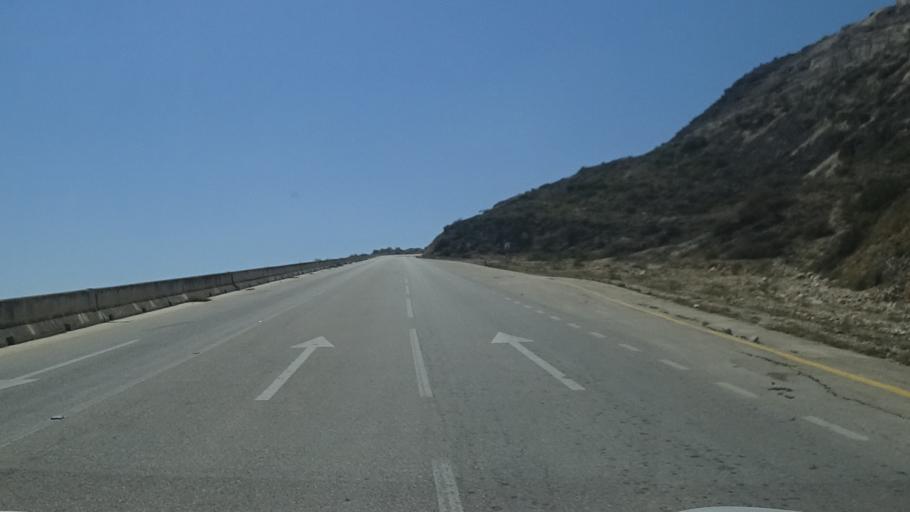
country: OM
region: Zufar
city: Salalah
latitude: 16.8311
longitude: 53.6715
